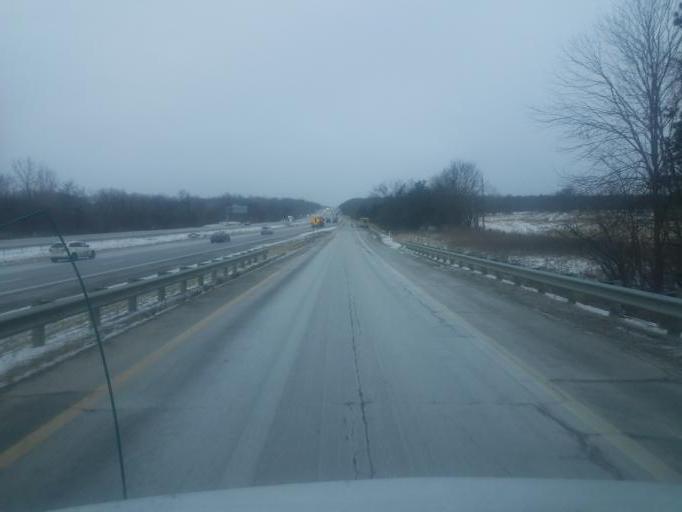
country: US
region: Ohio
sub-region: Morrow County
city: Mount Gilead
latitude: 40.4960
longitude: -82.7205
